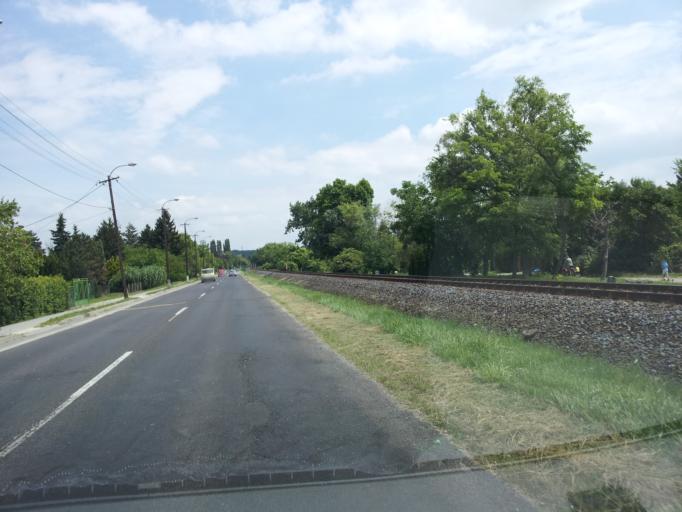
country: HU
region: Veszprem
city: Balatonkenese
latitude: 47.0327
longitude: 18.1169
